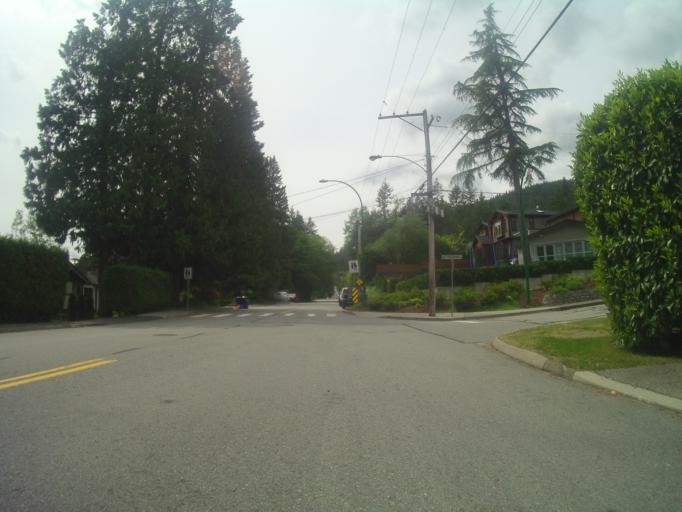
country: CA
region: British Columbia
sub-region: Fraser Valley Regional District
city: North Vancouver
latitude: 49.3479
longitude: -123.0304
